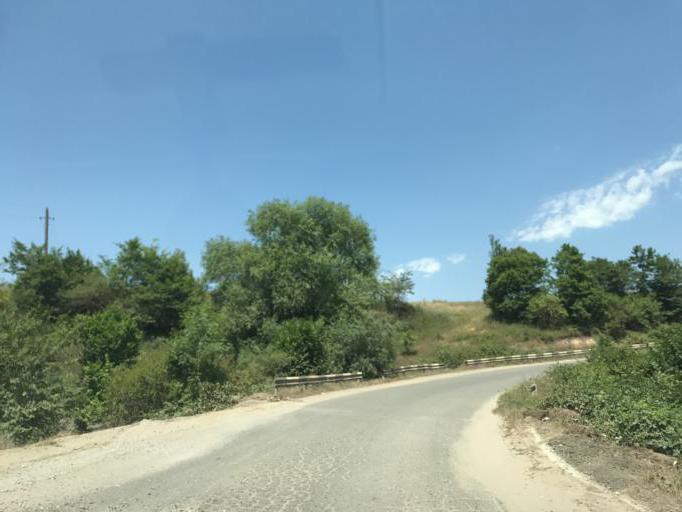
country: AZ
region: Tartar Rayon
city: Martakert
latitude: 40.1095
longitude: 46.6346
